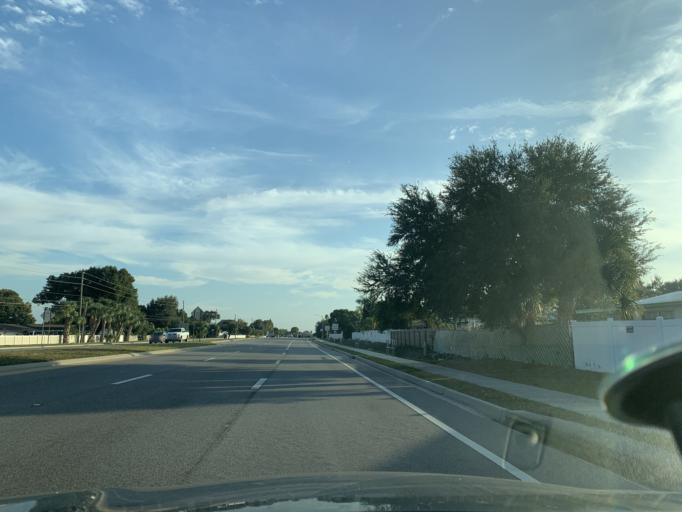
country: US
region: Florida
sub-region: Pinellas County
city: Ridgecrest
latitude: 27.8929
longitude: -82.7955
